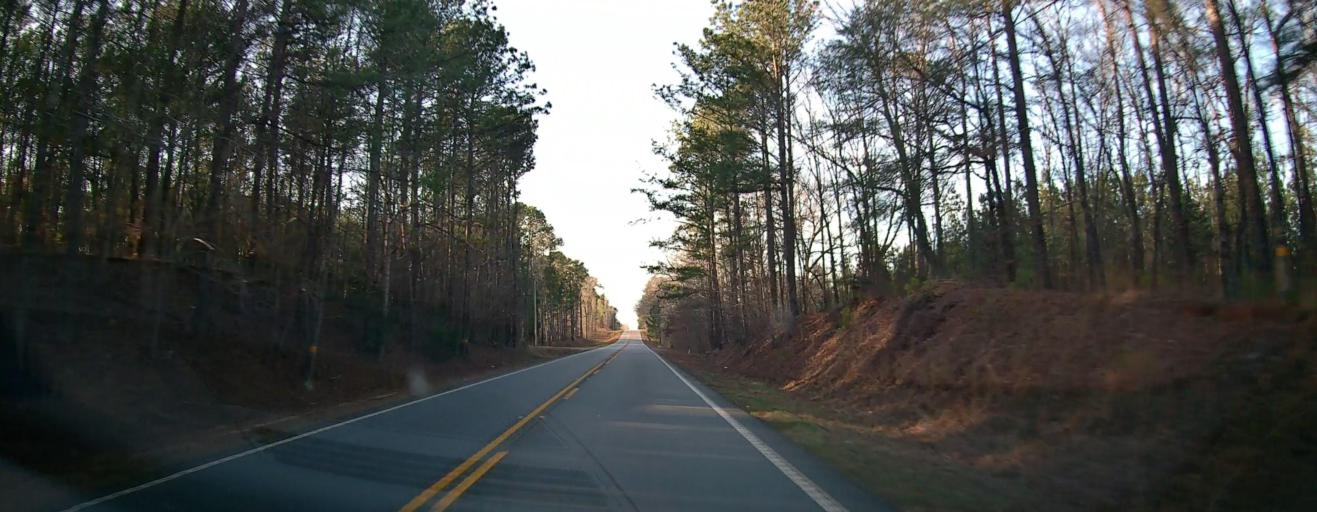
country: US
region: Alabama
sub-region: Chambers County
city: Valley
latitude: 32.7804
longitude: -85.0915
